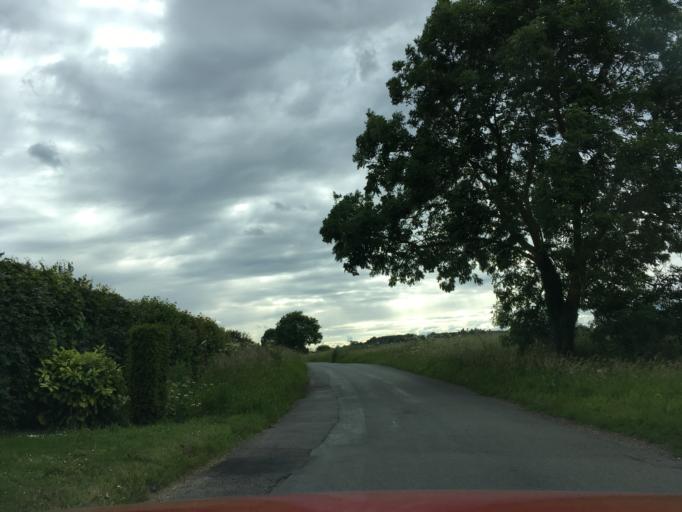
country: GB
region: England
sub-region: Oxfordshire
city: Boars Hill
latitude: 51.7032
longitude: -1.2691
